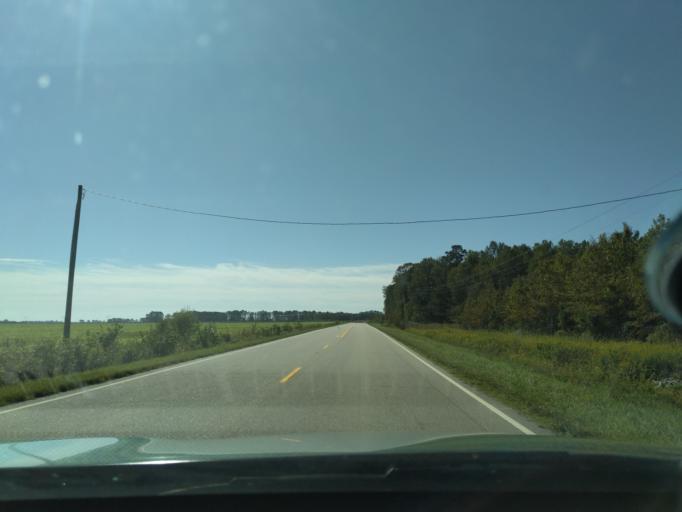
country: US
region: North Carolina
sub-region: Washington County
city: Plymouth
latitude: 35.7480
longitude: -76.7396
